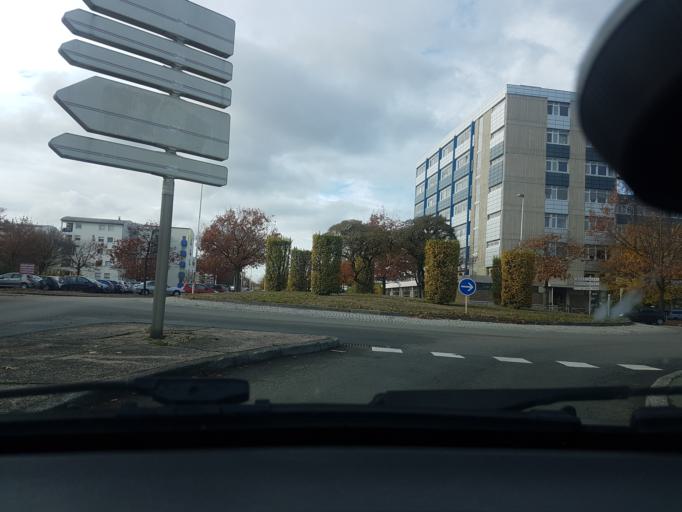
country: FR
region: Franche-Comte
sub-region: Departement du Doubs
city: Arbouans
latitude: 47.4991
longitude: 6.8032
